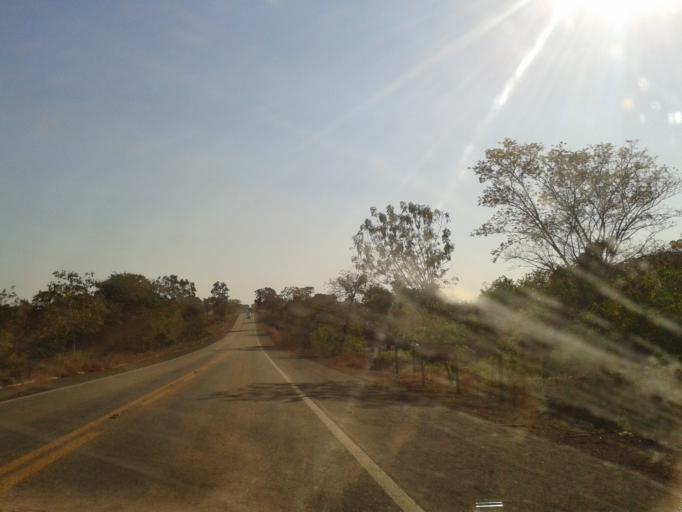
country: BR
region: Goias
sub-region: Mozarlandia
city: Mozarlandia
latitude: -15.0769
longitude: -50.6209
